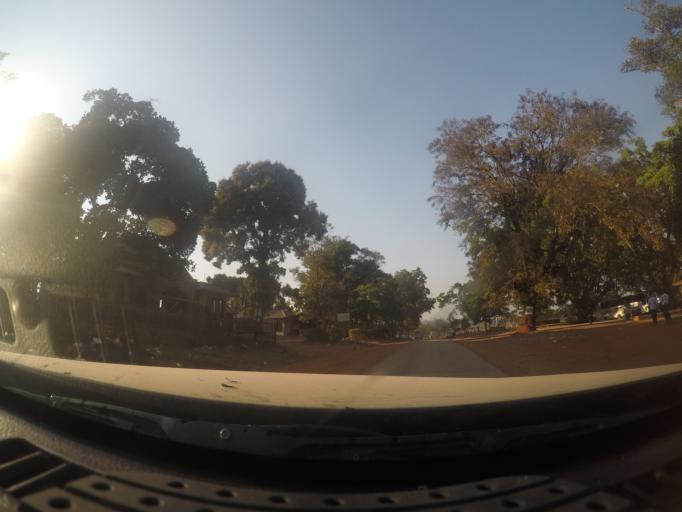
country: MM
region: Shan
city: Taunggyi
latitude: 20.4450
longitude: 97.1358
